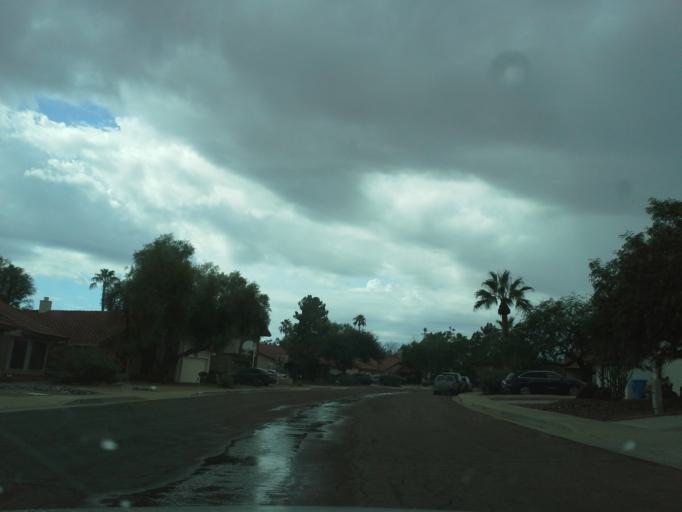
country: US
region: Arizona
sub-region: Maricopa County
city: Paradise Valley
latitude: 33.6171
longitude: -112.0388
